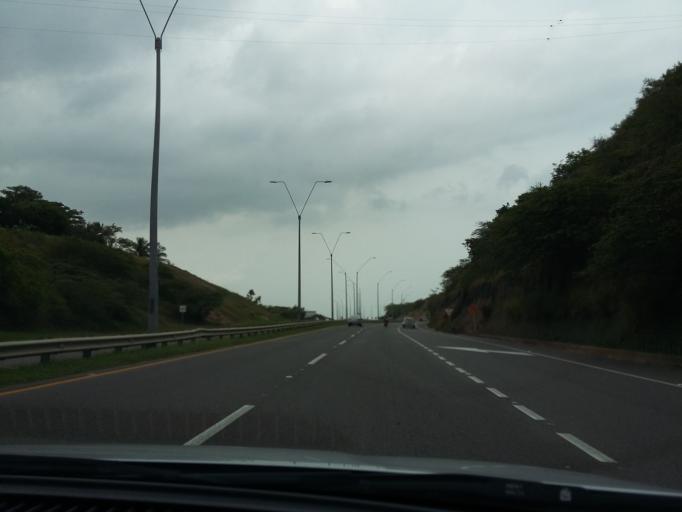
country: CO
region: Bolivar
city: Santa Rosa
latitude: 10.5143
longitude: -75.4697
